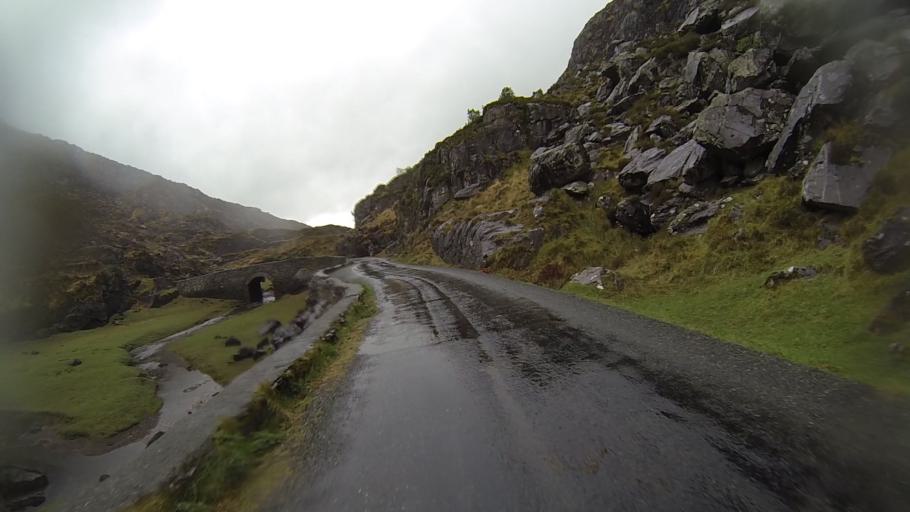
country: IE
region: Munster
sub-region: Ciarrai
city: Cill Airne
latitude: 52.0041
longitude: -9.6434
